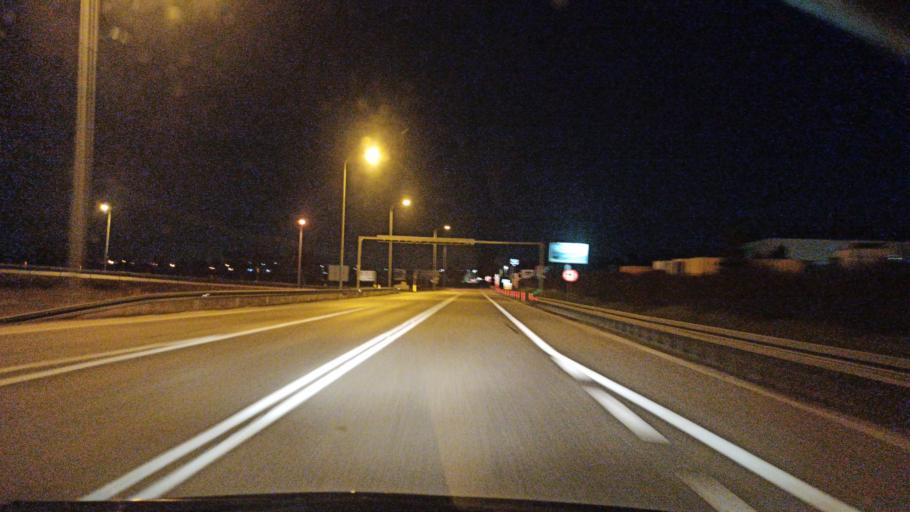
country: PL
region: Warmian-Masurian Voivodeship
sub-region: Powiat elblaski
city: Gronowo Gorne
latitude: 54.1391
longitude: 19.4493
